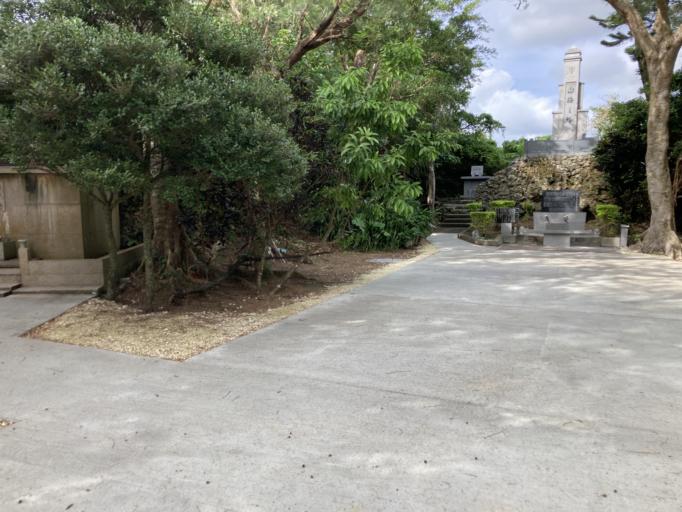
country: JP
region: Okinawa
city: Itoman
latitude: 26.1162
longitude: 127.6865
